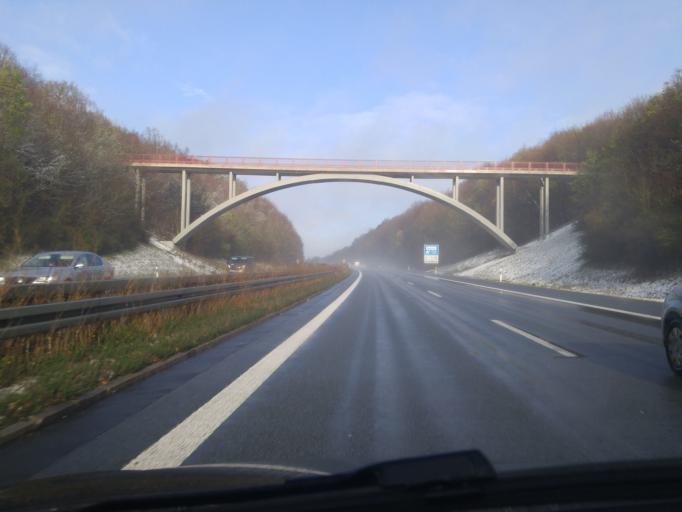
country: DE
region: Bavaria
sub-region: Regierungsbezirk Unterfranken
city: Unterpleichfeld
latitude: 49.8924
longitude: 10.0009
